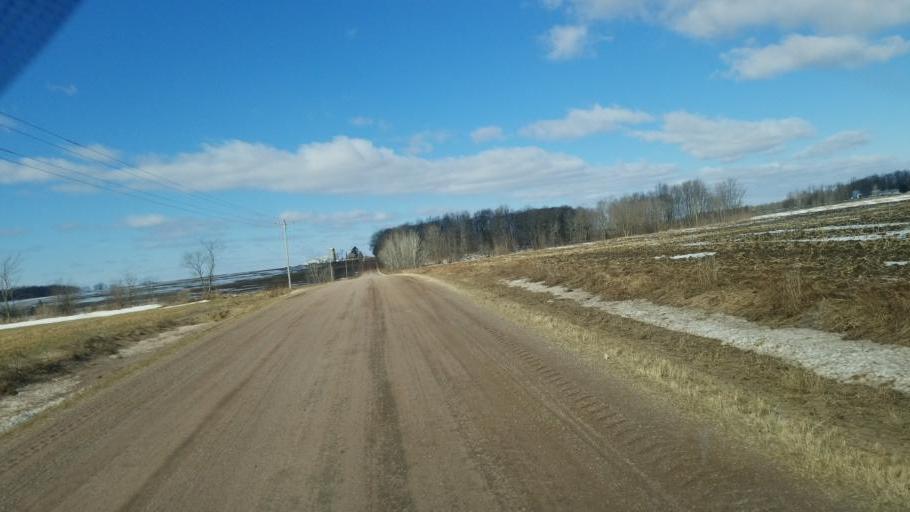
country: US
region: Wisconsin
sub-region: Clark County
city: Loyal
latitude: 44.6834
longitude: -90.4495
